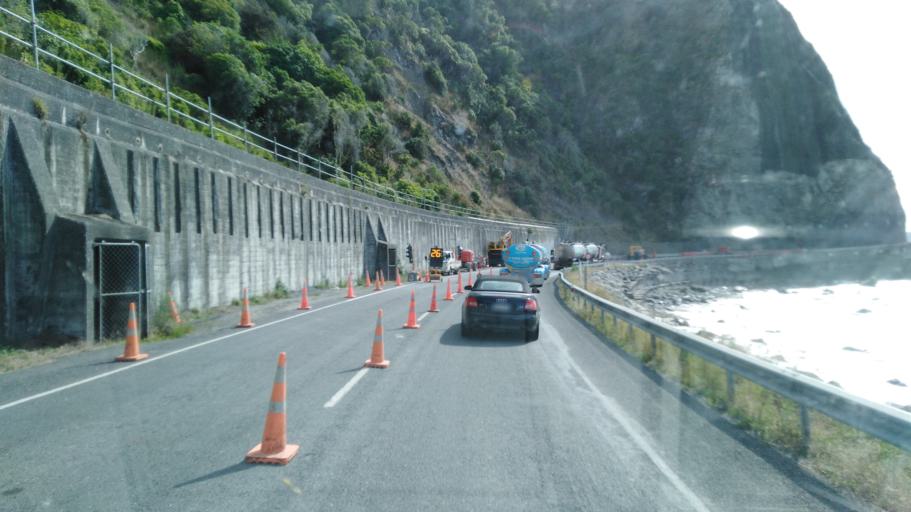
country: NZ
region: Canterbury
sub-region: Kaikoura District
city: Kaikoura
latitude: -42.4453
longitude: 173.5833
